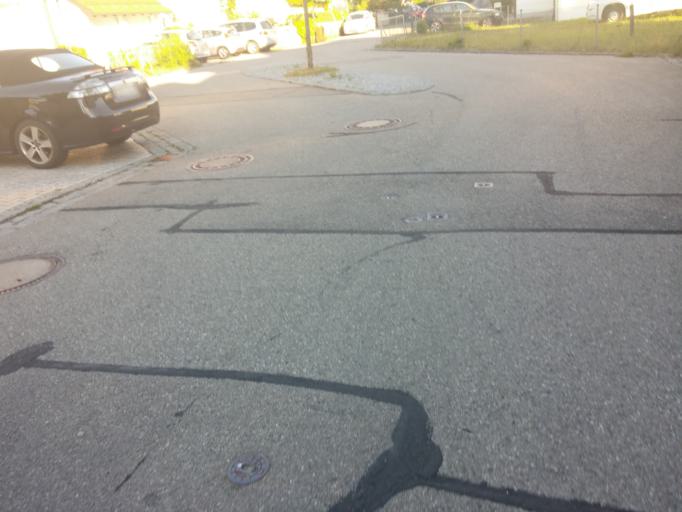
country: DE
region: Bavaria
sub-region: Upper Bavaria
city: Aschheim
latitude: 48.1692
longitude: 11.7229
